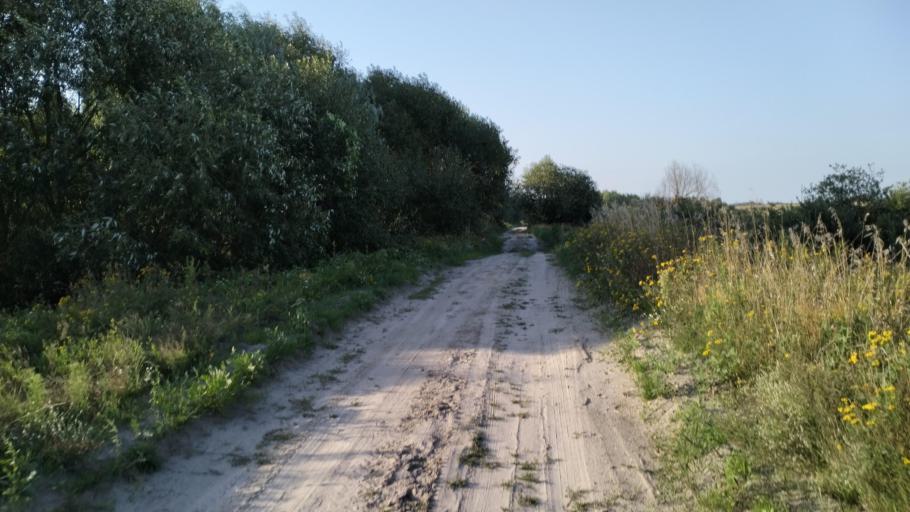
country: BY
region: Brest
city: Davyd-Haradok
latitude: 52.0258
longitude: 27.1944
